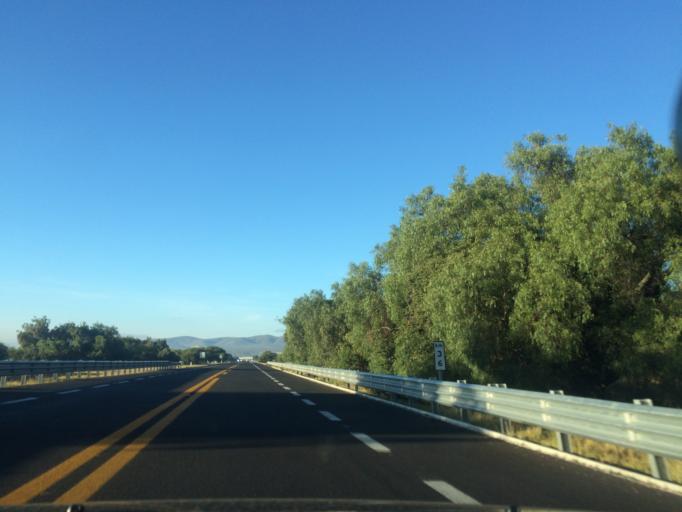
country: MX
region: Puebla
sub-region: Santiago Miahuatlan
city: San Jose Monte Chiquito
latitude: 18.5200
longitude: -97.4544
